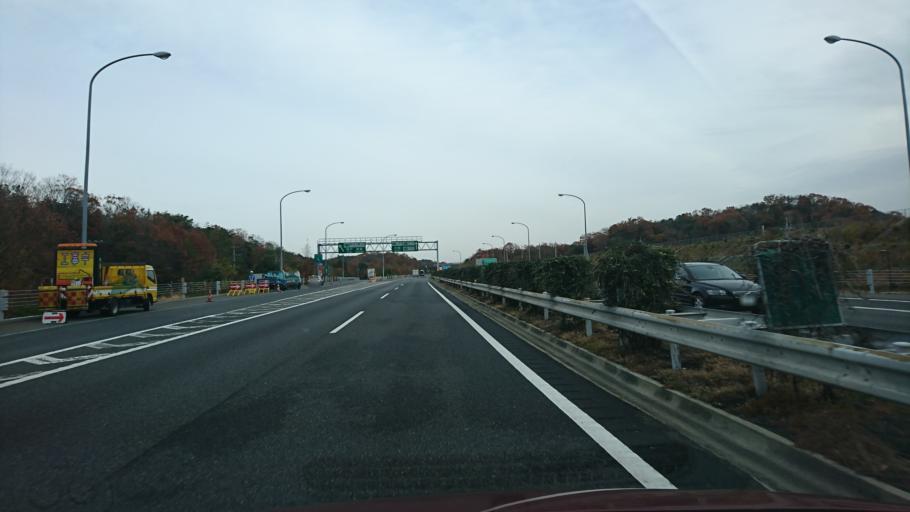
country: JP
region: Hyogo
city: Miki
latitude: 34.8074
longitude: 135.0714
